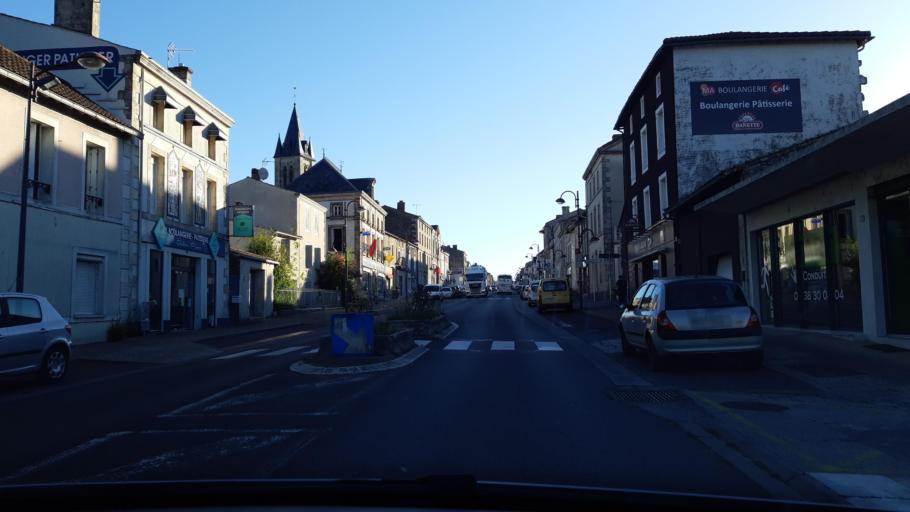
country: FR
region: Poitou-Charentes
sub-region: Departement des Deux-Sevres
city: La Creche
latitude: 46.3602
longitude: -0.3014
